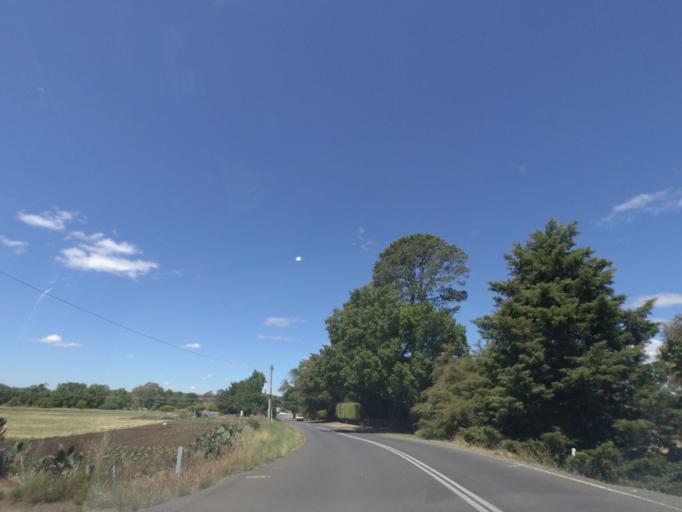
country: AU
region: Victoria
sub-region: Mount Alexander
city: Castlemaine
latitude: -37.2381
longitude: 144.4165
